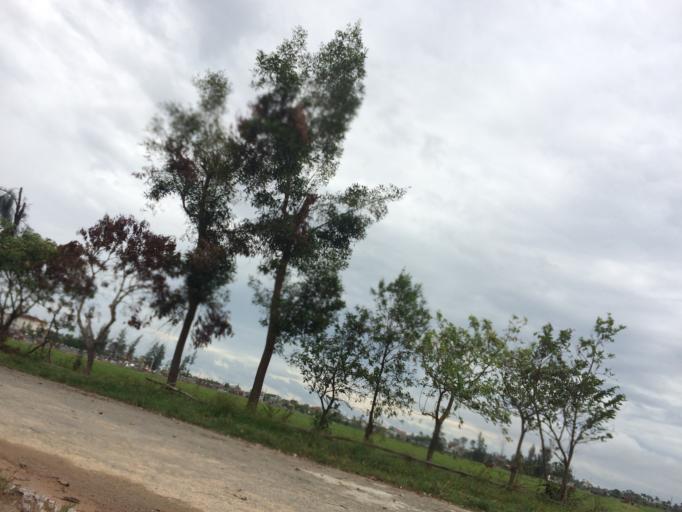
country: VN
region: Ha Tinh
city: Ha Tinh
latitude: 18.3601
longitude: 105.8921
